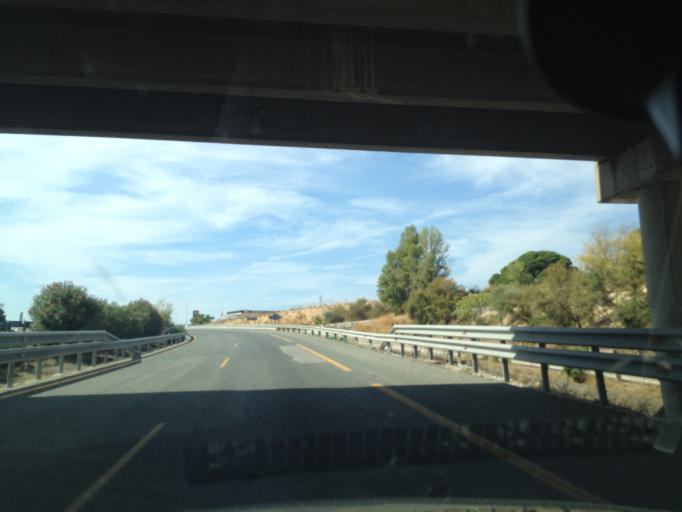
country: ES
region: Andalusia
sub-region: Provincia de Sevilla
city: La Puebla de Cazalla
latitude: 37.2316
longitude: -5.3210
